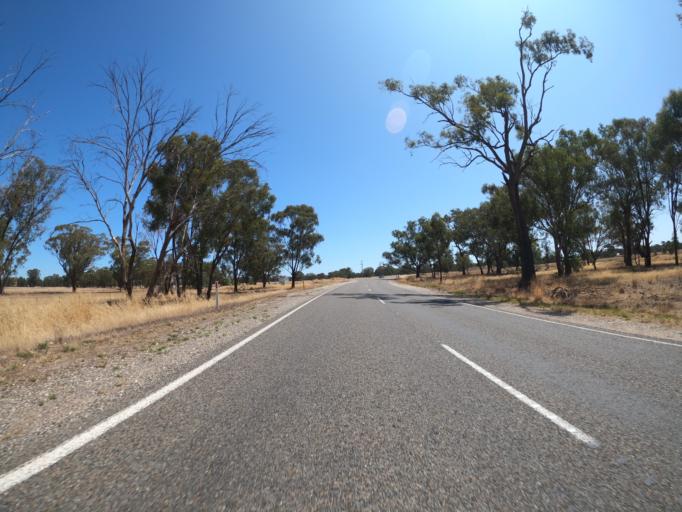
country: AU
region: New South Wales
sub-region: Corowa Shire
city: Corowa
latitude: -36.0835
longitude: 146.3338
